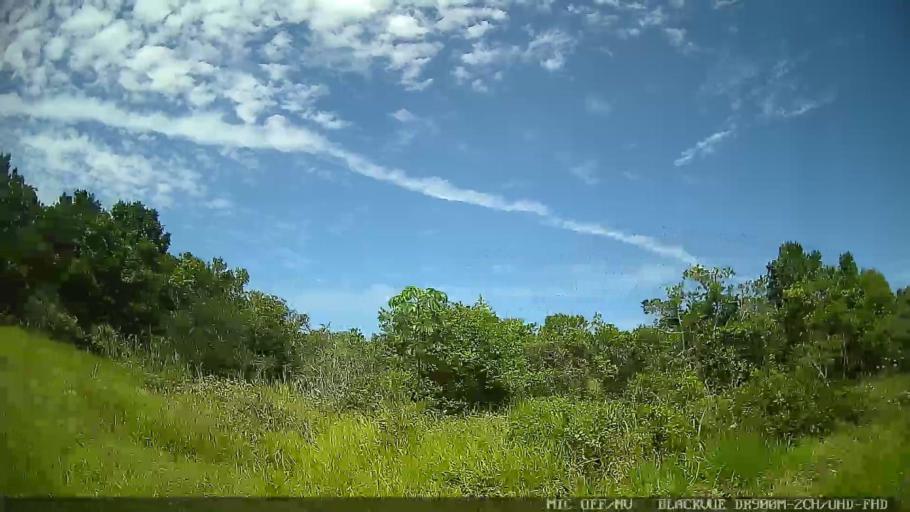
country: BR
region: Sao Paulo
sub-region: Iguape
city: Iguape
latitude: -24.7149
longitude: -47.5176
